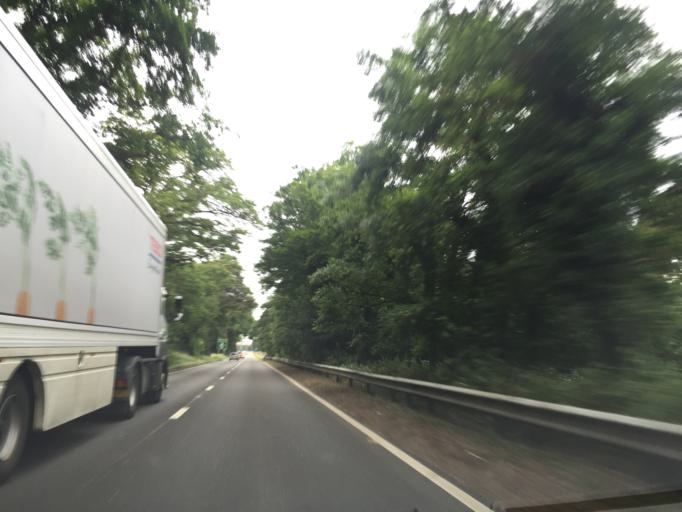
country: GB
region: England
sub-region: Dorset
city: St Leonards
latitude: 50.8231
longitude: -1.8499
